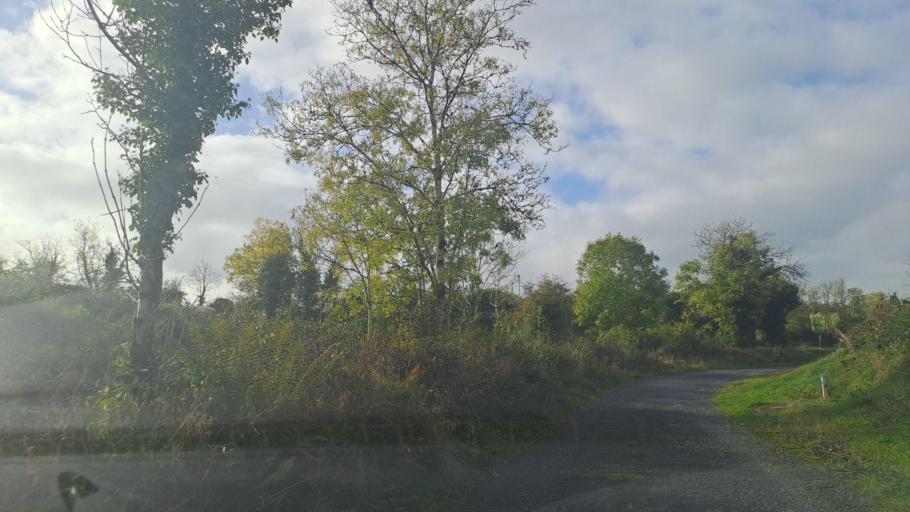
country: IE
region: Ulster
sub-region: An Cabhan
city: Kingscourt
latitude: 54.0034
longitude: -6.8192
